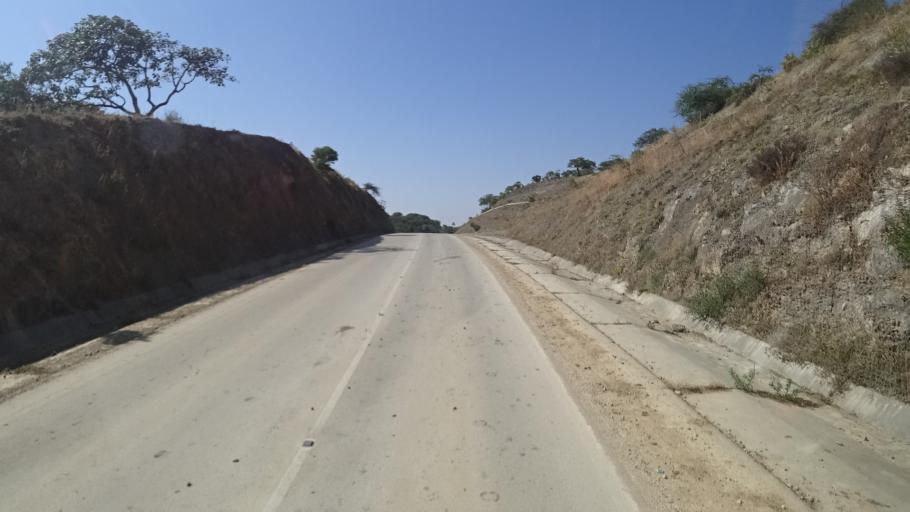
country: OM
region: Zufar
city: Salalah
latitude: 17.0623
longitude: 54.6052
